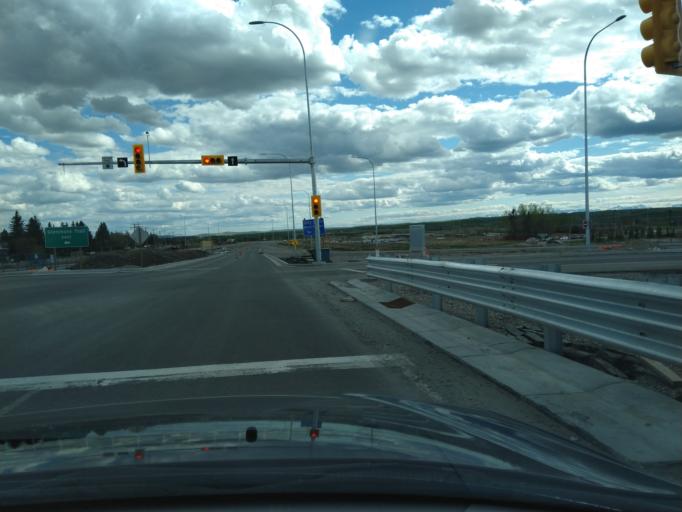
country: CA
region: Alberta
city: Calgary
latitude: 51.0083
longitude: -114.1417
